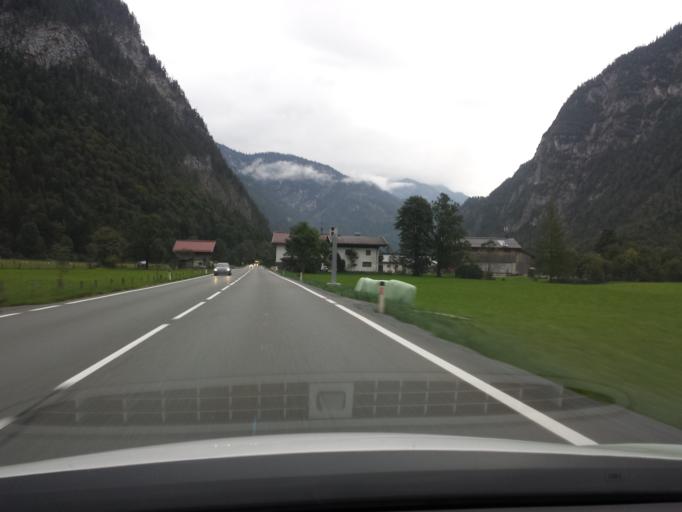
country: AT
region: Salzburg
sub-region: Politischer Bezirk Zell am See
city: Leogang
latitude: 47.4974
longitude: 12.7968
